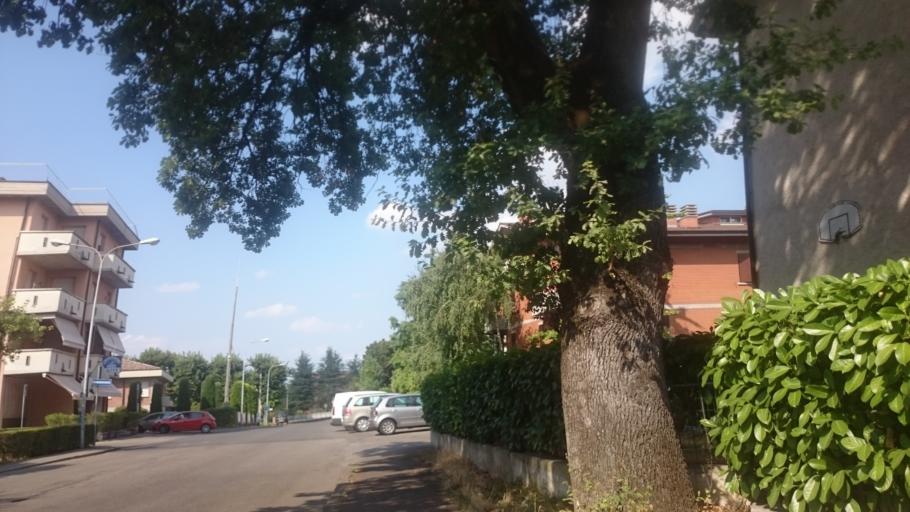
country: IT
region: Emilia-Romagna
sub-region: Provincia di Reggio Emilia
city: Scandiano
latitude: 44.5958
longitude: 10.6951
